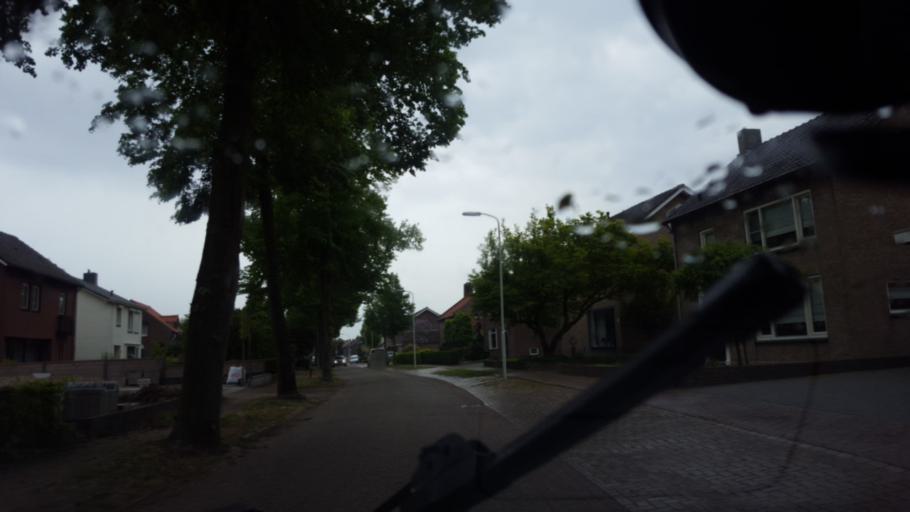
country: NL
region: North Brabant
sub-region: Gemeente Someren
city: Someren
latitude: 51.4217
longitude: 5.6794
